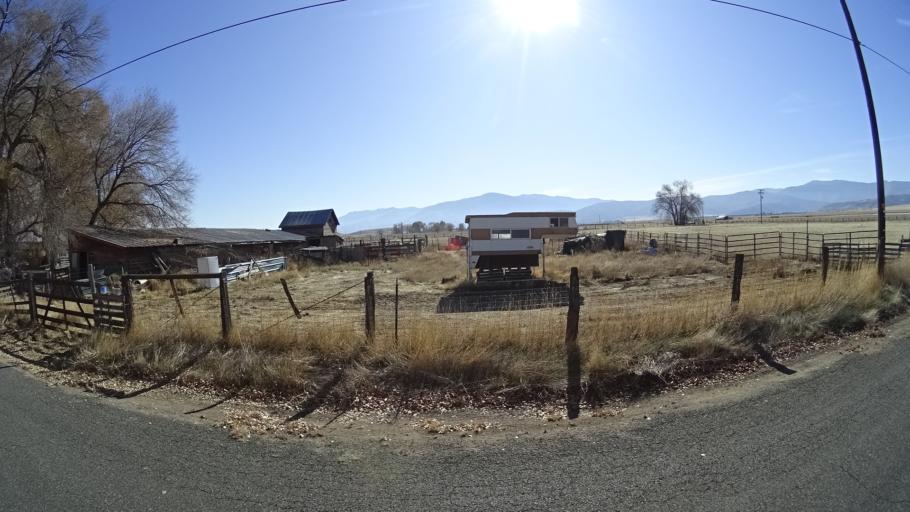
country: US
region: California
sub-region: Siskiyou County
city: Montague
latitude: 41.5747
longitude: -122.5268
